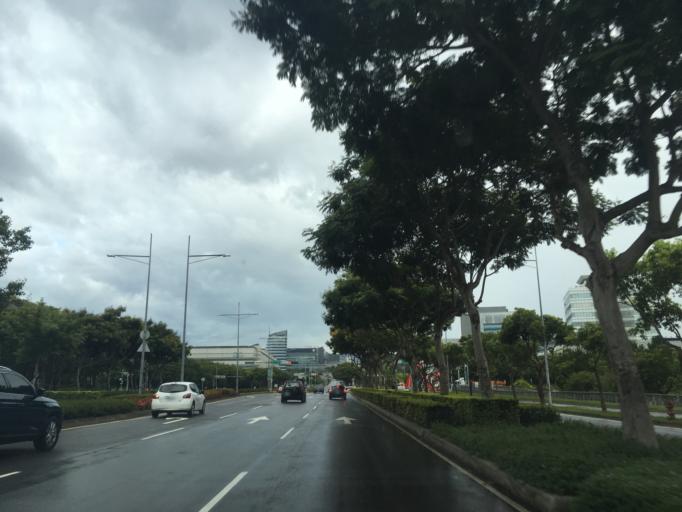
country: TW
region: Taiwan
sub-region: Taichung City
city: Taichung
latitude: 24.2079
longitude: 120.6207
